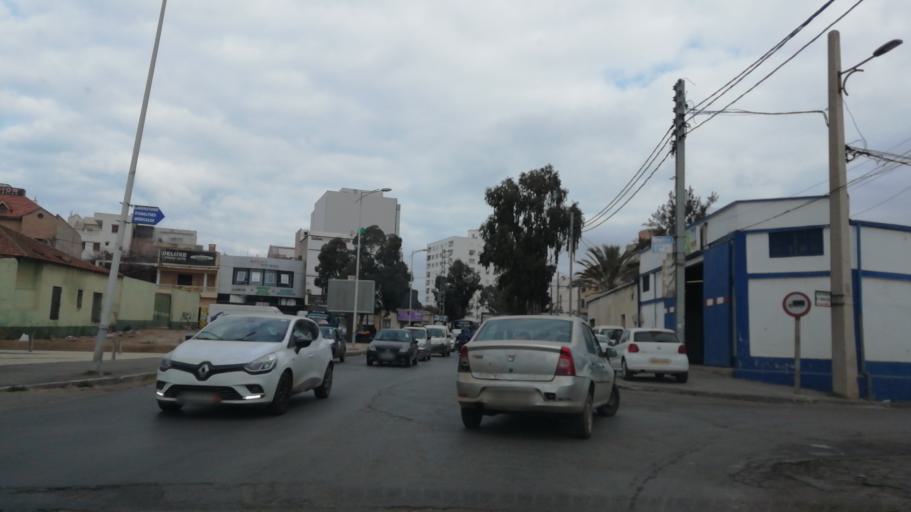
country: DZ
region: Oran
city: Oran
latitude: 35.7023
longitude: -0.6110
